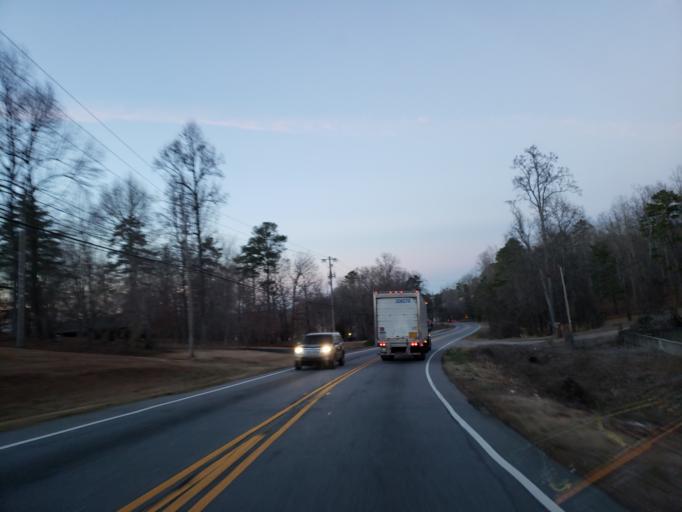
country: US
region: Georgia
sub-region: Cobb County
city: Powder Springs
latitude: 33.9426
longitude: -84.7045
